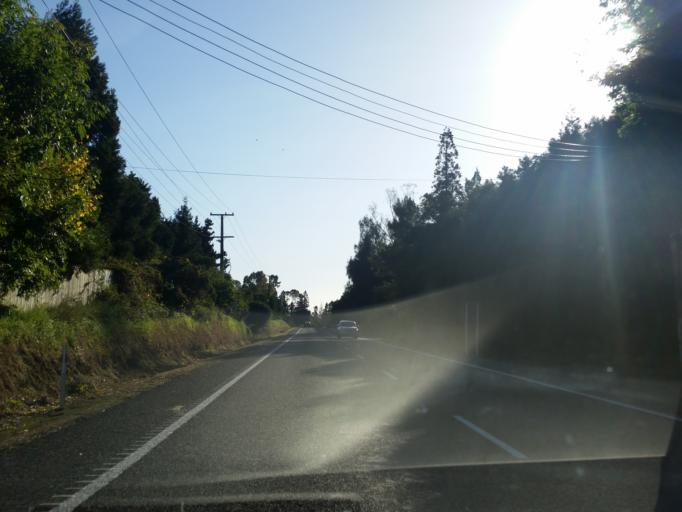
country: NZ
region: Bay of Plenty
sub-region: Western Bay of Plenty District
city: Katikati
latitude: -37.4862
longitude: 175.9298
